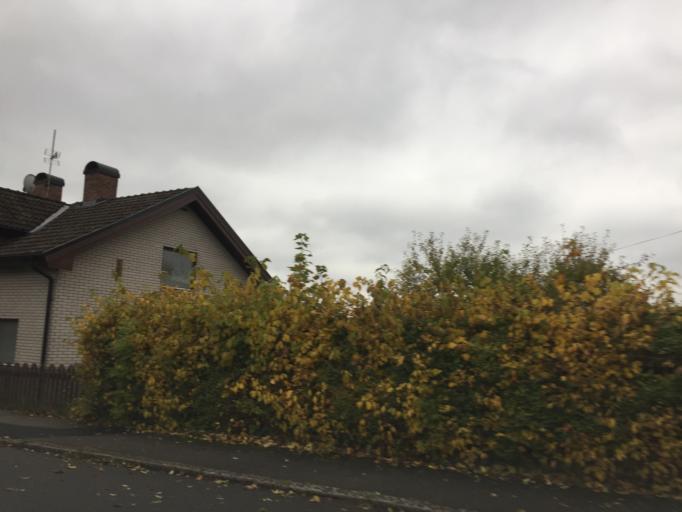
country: SE
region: Vaestra Goetaland
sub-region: Trollhattan
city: Trollhattan
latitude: 58.2821
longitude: 12.2734
